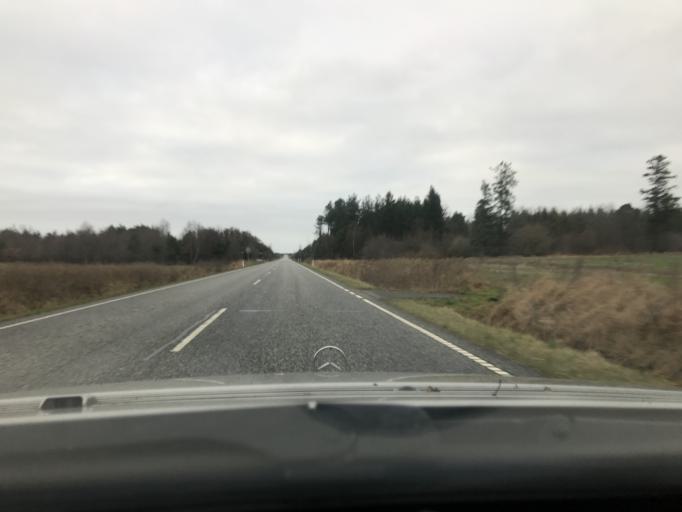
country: DK
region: South Denmark
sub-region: Tonder Kommune
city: Sherrebek
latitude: 55.1756
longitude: 8.8419
